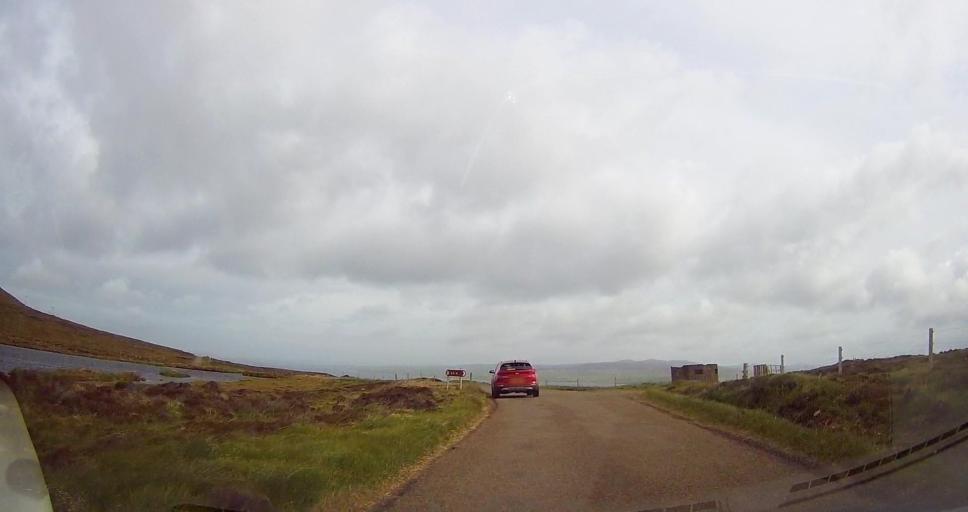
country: GB
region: Scotland
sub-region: Orkney Islands
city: Stromness
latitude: 58.8803
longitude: -3.2482
